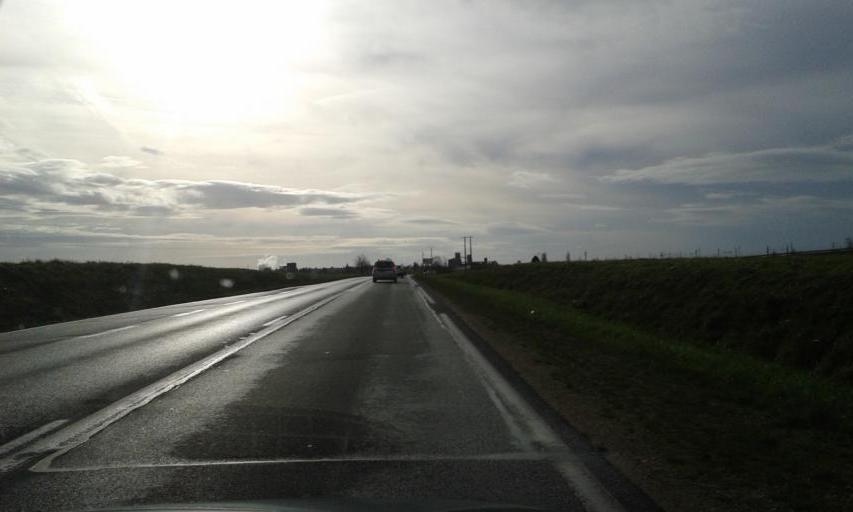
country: FR
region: Centre
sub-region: Departement du Loiret
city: Baule
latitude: 47.7958
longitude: 1.6512
